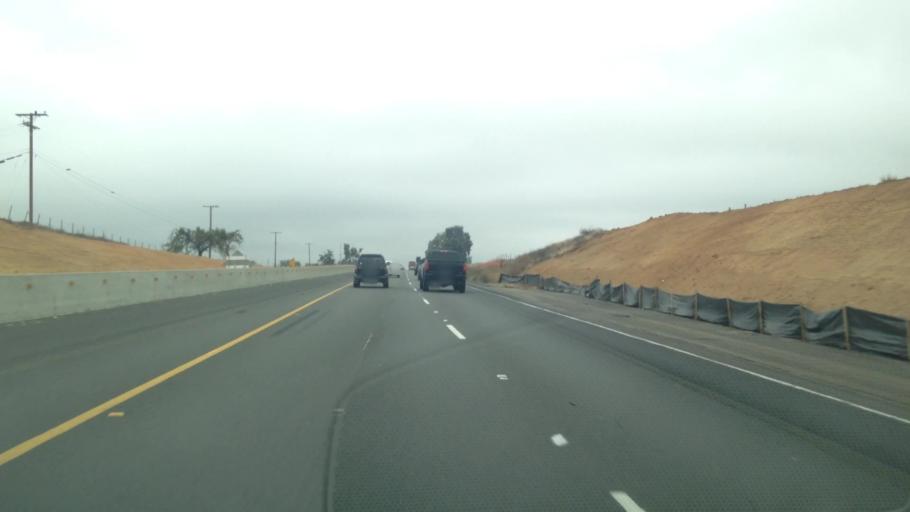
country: US
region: California
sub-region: Riverside County
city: Beaumont
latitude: 33.9336
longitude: -117.0159
